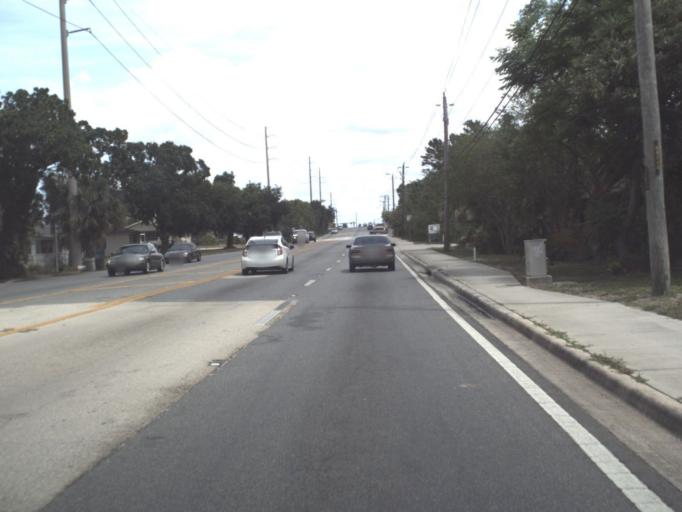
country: US
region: Florida
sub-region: Brevard County
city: Cocoa
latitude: 28.3897
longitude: -80.7550
